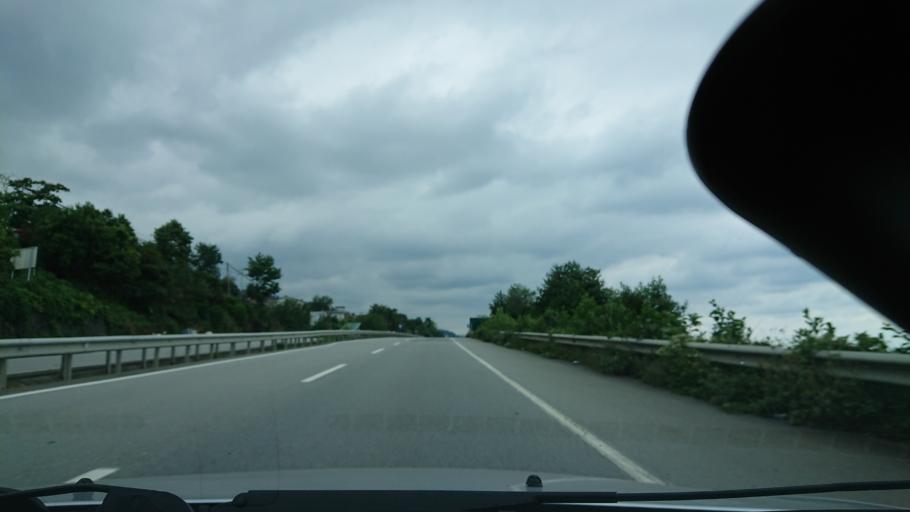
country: TR
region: Giresun
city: Eynesil
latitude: 41.0504
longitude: 39.1149
